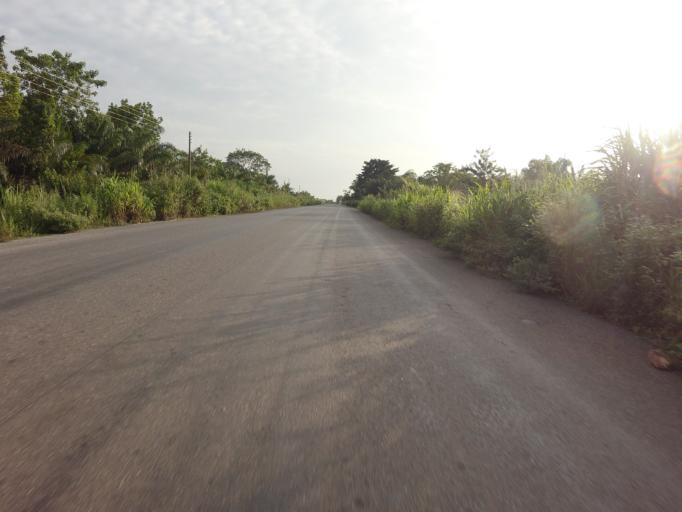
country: GH
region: Volta
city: Kpandu
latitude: 6.9057
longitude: 0.4429
